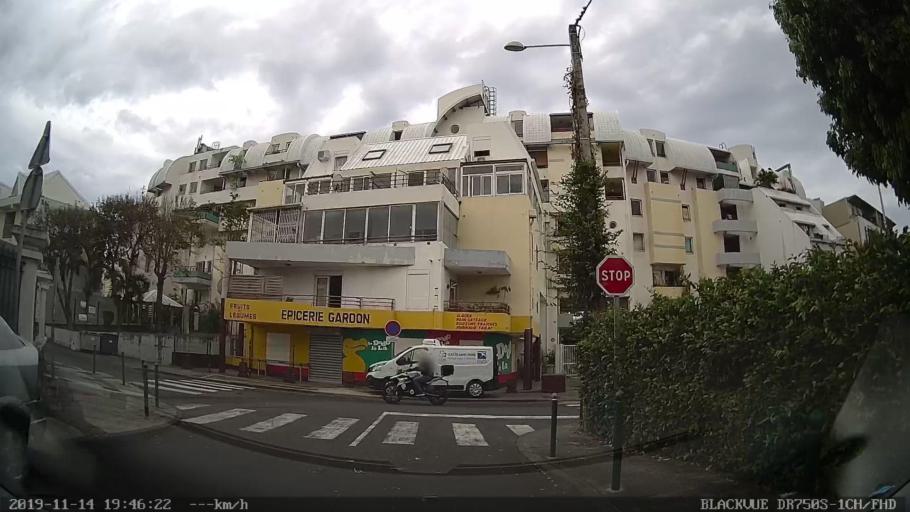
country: RE
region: Reunion
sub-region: Reunion
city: Saint-Denis
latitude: -20.8890
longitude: 55.4575
